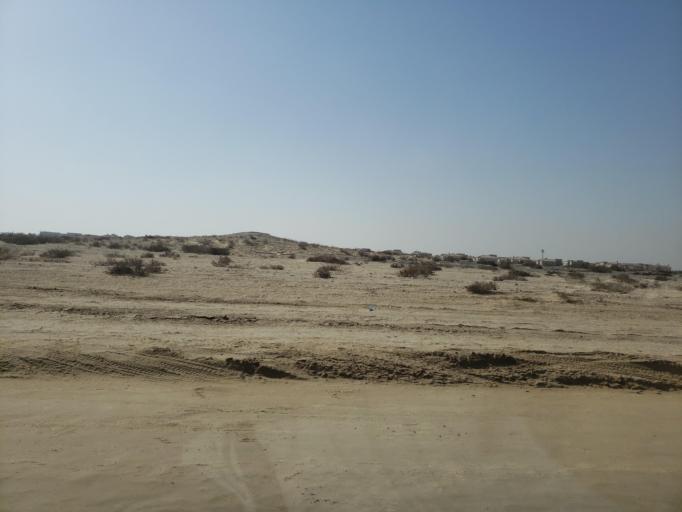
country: AE
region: Umm al Qaywayn
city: Umm al Qaywayn
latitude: 25.5315
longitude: 55.5948
